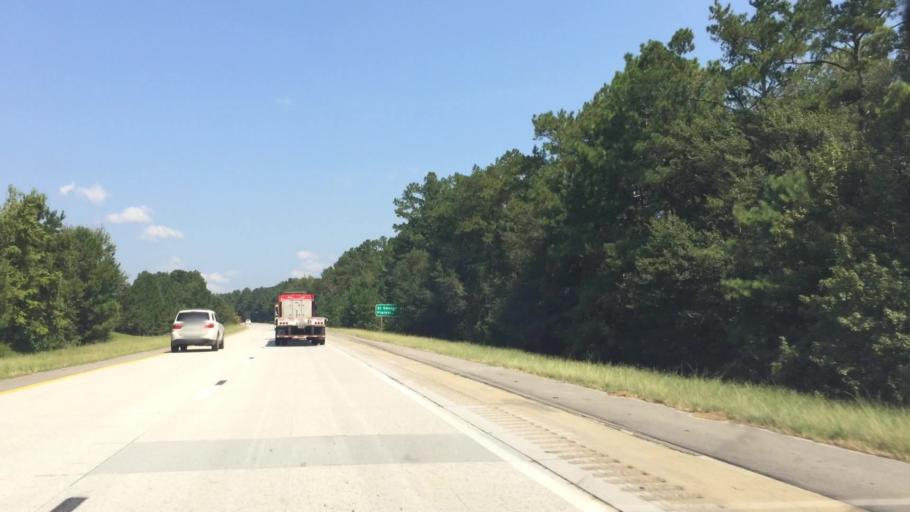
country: US
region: South Carolina
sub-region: Dorchester County
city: Saint George
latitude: 33.0956
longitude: -80.6469
